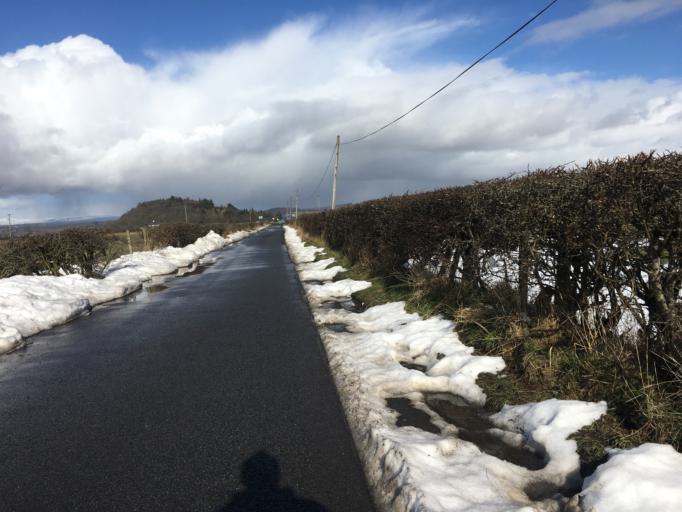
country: GB
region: Scotland
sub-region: Stirling
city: Stirling
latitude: 56.1167
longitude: -3.9743
